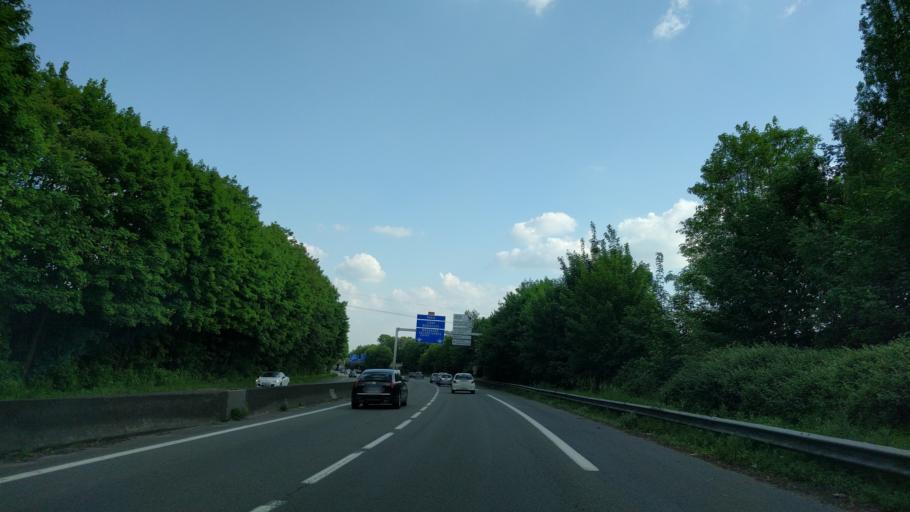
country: FR
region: Nord-Pas-de-Calais
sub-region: Departement du Nord
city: La Sentinelle
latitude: 50.3500
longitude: 3.4790
